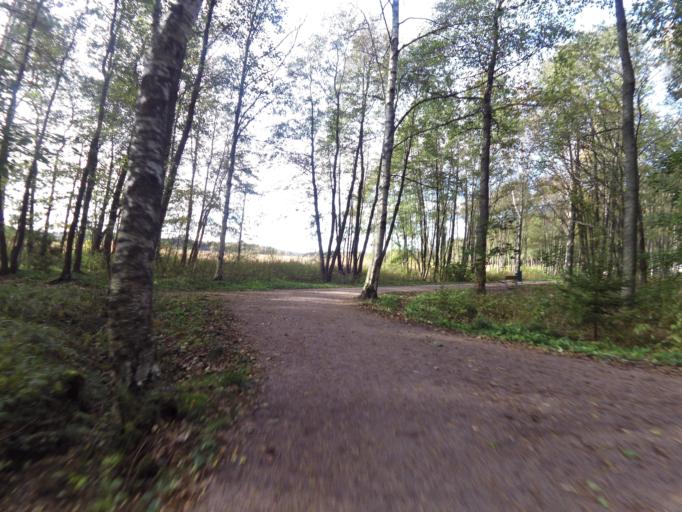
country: FI
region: Uusimaa
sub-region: Helsinki
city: Koukkuniemi
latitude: 60.1429
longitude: 24.7012
